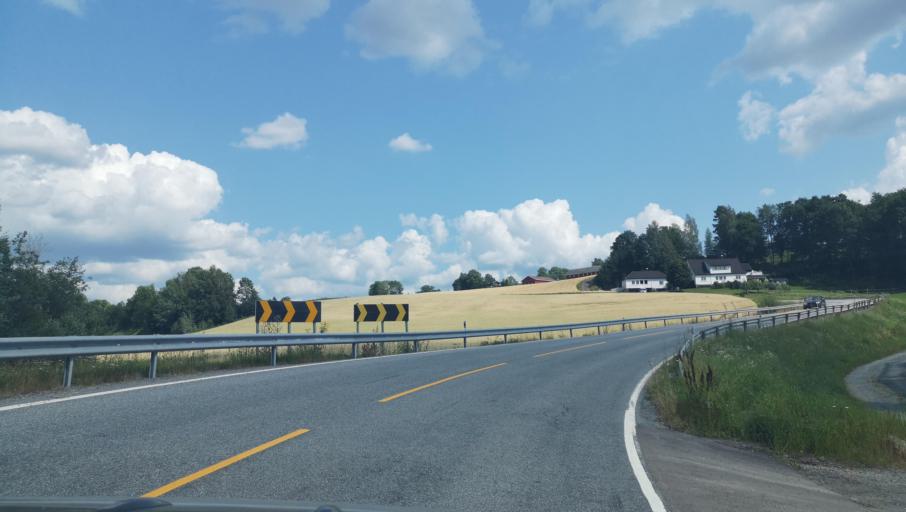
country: NO
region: Buskerud
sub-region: Ovre Eiker
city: Hokksund
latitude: 59.7260
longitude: 9.8346
